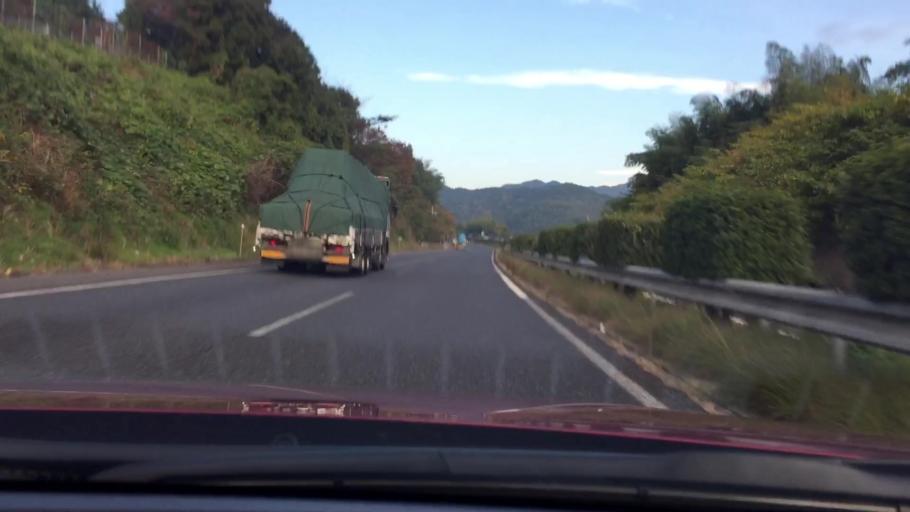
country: JP
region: Hyogo
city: Yamazakicho-nakabirose
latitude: 34.9651
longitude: 134.6784
